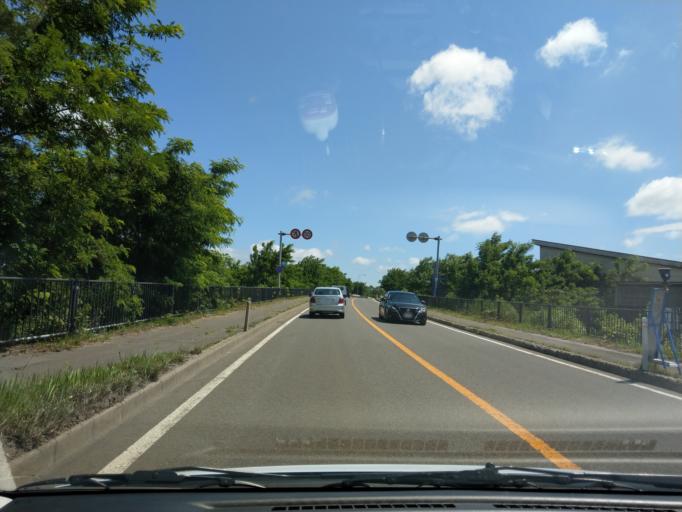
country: JP
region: Akita
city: Odate
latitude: 40.2921
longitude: 140.5633
